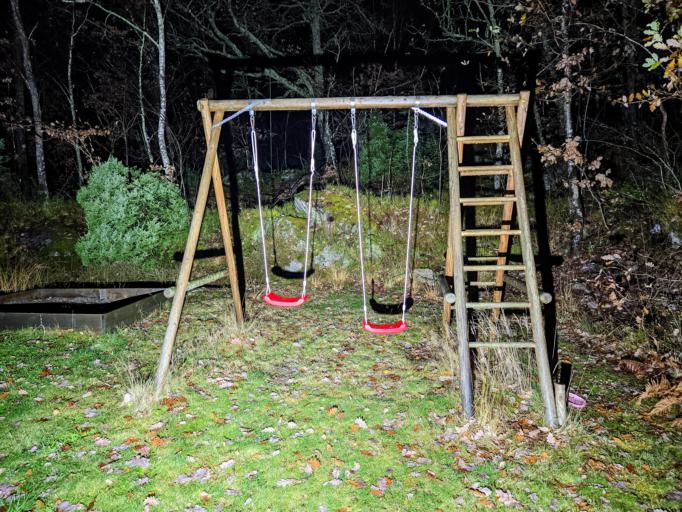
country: NO
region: Rogaland
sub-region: Hjelmeland
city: Hjelmelandsvagen
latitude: 59.2721
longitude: 6.1526
